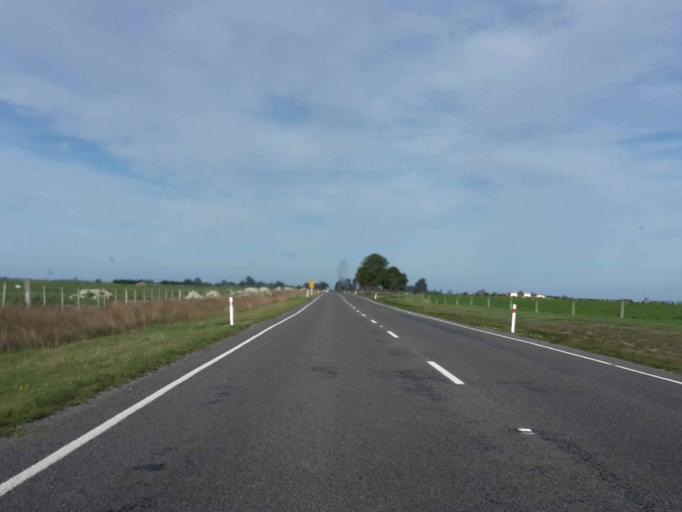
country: NZ
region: Canterbury
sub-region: Timaru District
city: Pleasant Point
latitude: -44.0546
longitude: 171.3409
